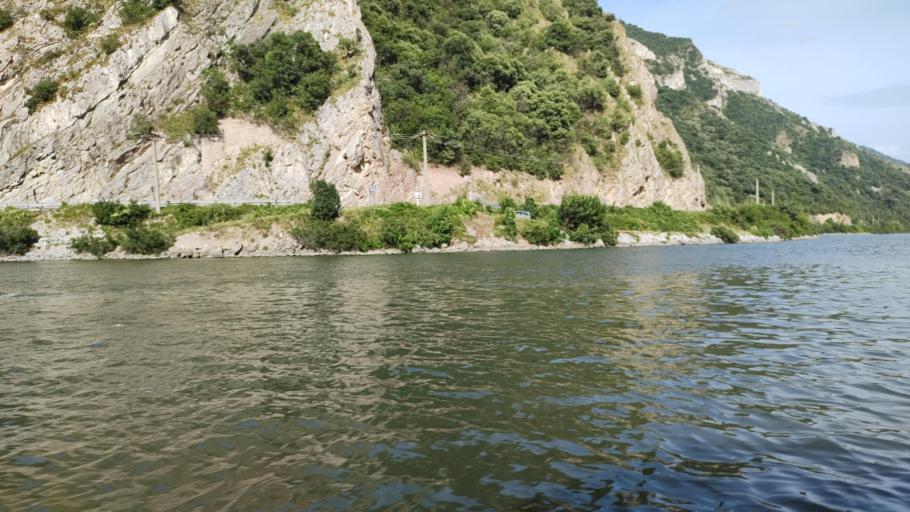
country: RO
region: Caras-Severin
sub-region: Comuna Berzasca
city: Berzasca
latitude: 44.6105
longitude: 22.0048
